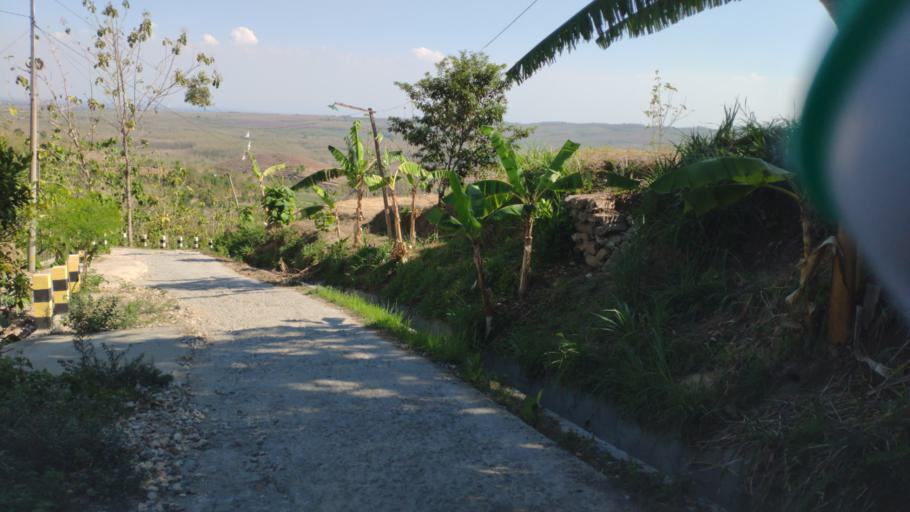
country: ID
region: East Java
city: Kedewan
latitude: -7.0185
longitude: 111.5814
